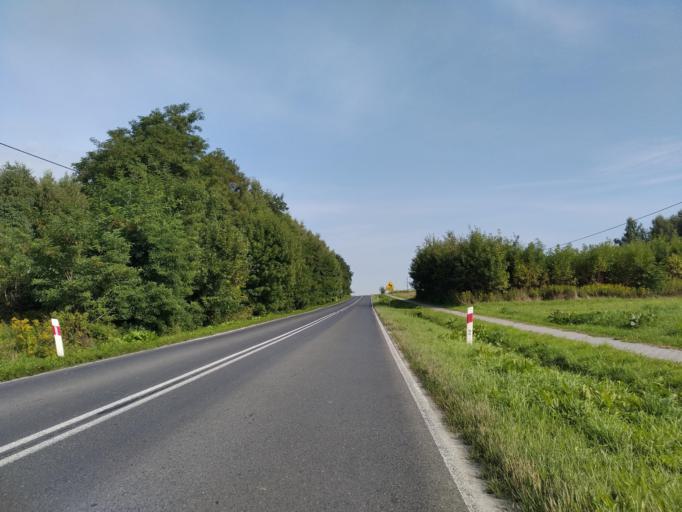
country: PL
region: Subcarpathian Voivodeship
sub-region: Powiat ropczycko-sedziszowski
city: Ostrow
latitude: 50.1029
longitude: 21.5934
